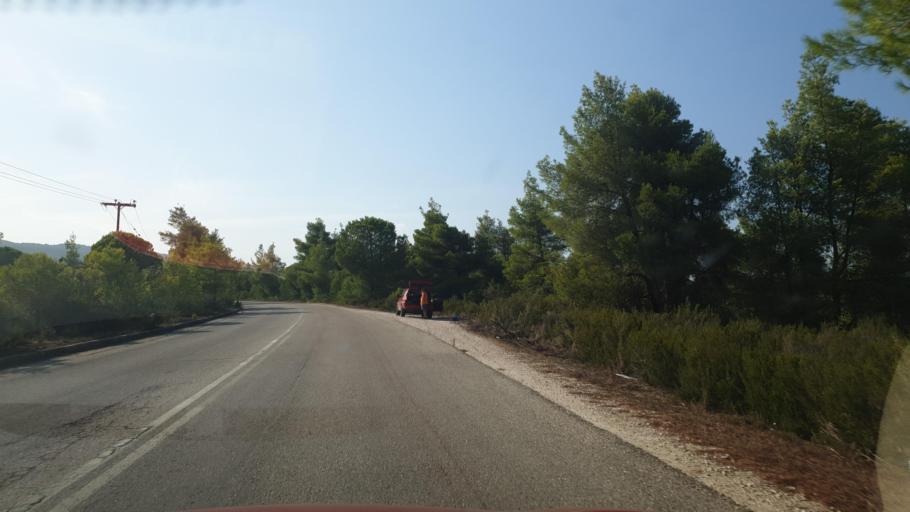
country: GR
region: Central Macedonia
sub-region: Nomos Chalkidikis
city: Sarti
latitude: 40.1274
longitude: 23.9442
